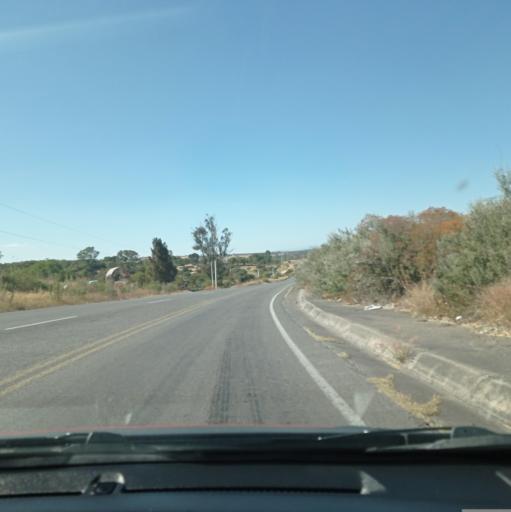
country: MX
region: Jalisco
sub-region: San Julian
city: Colonia Veintitres de Mayo
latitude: 21.0029
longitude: -102.2760
